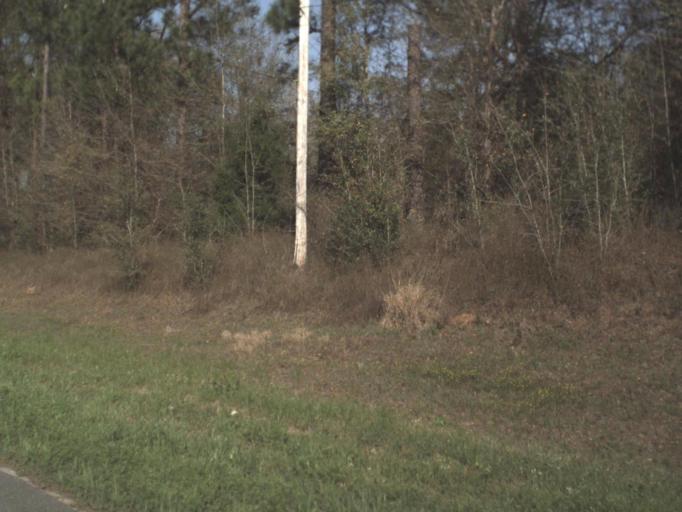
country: US
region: Alabama
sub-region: Houston County
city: Cottonwood
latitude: 30.9466
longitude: -85.3855
